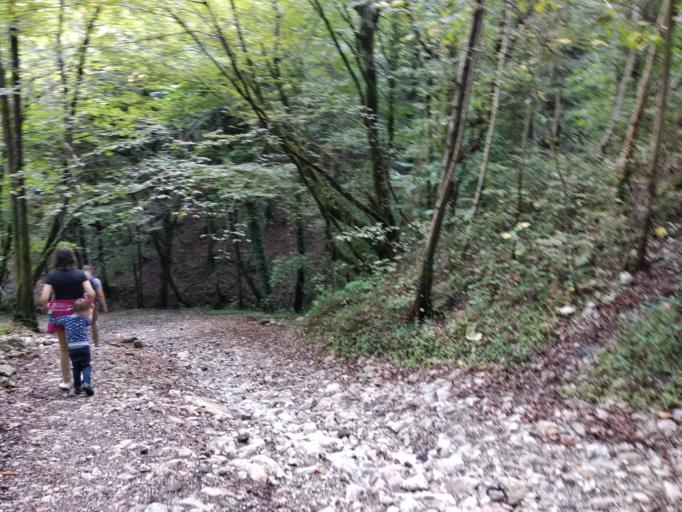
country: RU
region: Krasnodarskiy
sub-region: Sochi City
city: Sochi
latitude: 43.6351
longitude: 39.8171
